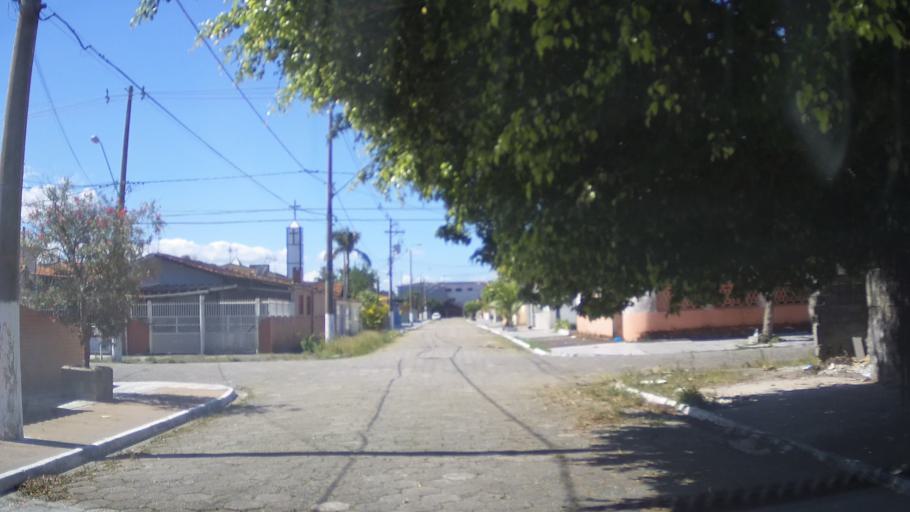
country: BR
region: Sao Paulo
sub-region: Praia Grande
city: Praia Grande
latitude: -24.0378
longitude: -46.5064
